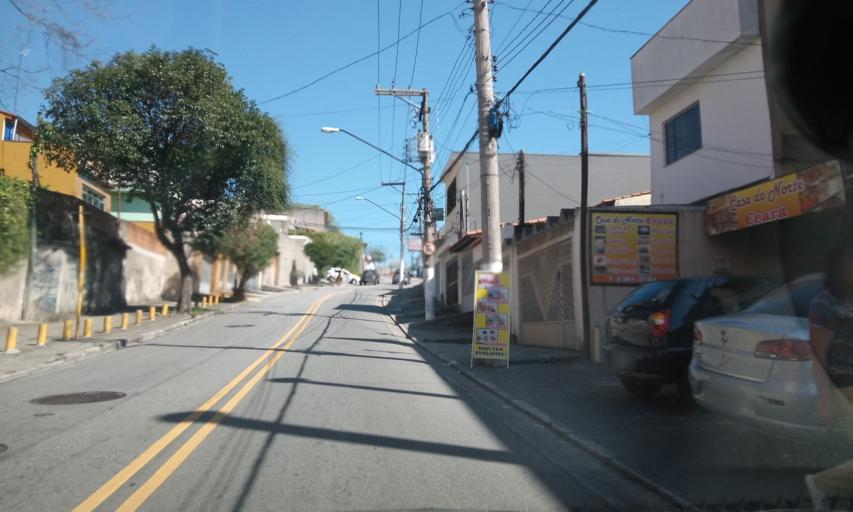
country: BR
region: Sao Paulo
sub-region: Sao Bernardo Do Campo
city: Sao Bernardo do Campo
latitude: -23.7231
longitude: -46.5698
